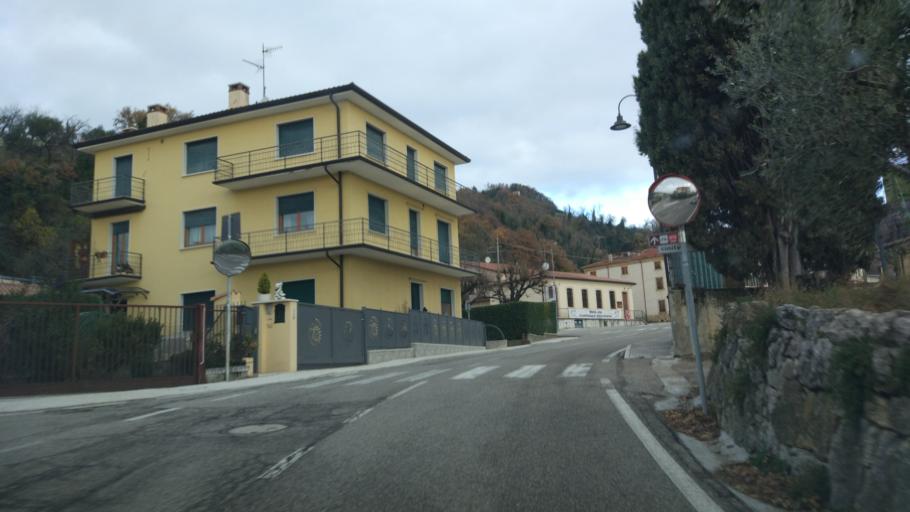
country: IT
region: Veneto
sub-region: Provincia di Verona
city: Marano di Valpolicella
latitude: 45.5551
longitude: 10.9155
